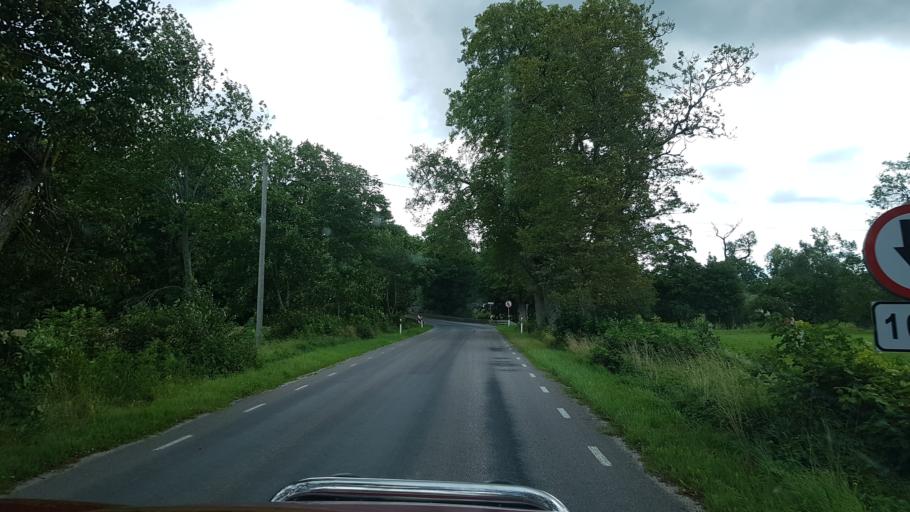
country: EE
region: Laeaene
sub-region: Lihula vald
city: Lihula
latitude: 58.7073
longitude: 24.0230
